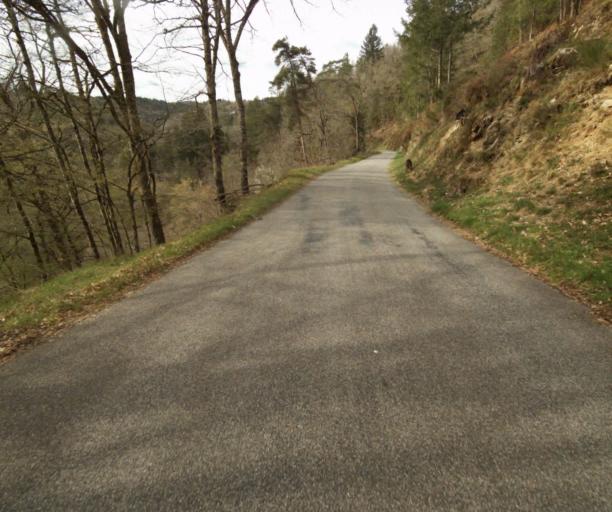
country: FR
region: Limousin
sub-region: Departement de la Correze
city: Argentat
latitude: 45.1926
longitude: 1.9804
